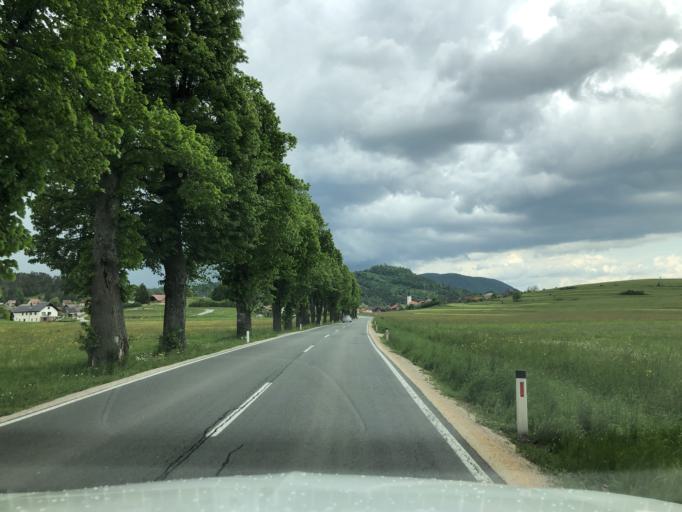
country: SI
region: Cerknica
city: Rakek
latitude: 45.8162
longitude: 14.3009
